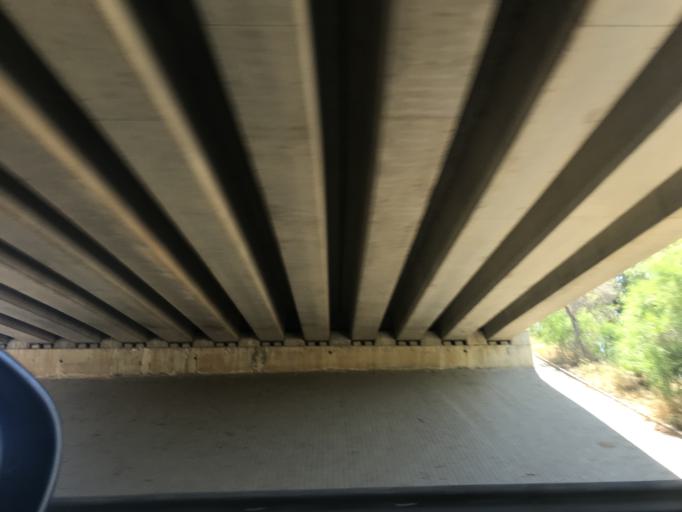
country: TR
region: Aydin
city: Aydin
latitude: 37.8188
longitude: 27.8469
